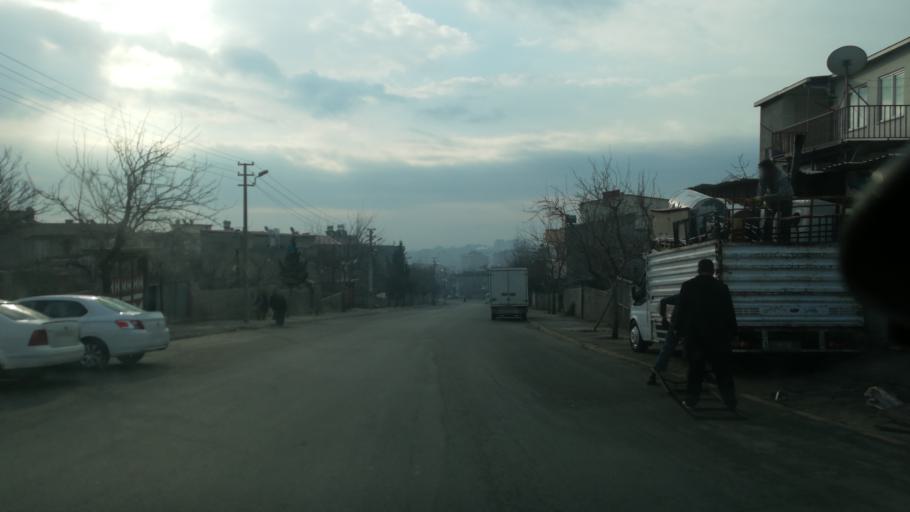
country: TR
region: Kahramanmaras
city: Kahramanmaras
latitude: 37.5935
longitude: 36.9051
